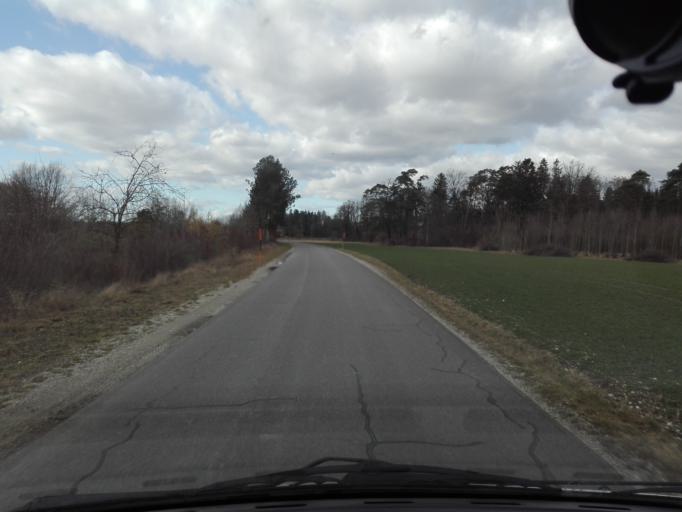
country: AT
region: Upper Austria
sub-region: Politischer Bezirk Perg
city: Perg
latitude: 48.2114
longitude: 14.6805
